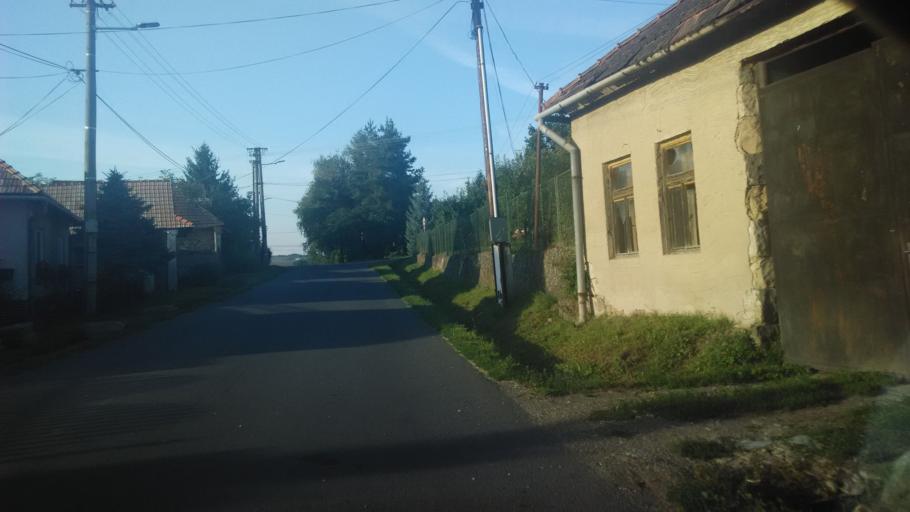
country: SK
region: Banskobystricky
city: Dudince
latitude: 48.1874
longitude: 18.8516
